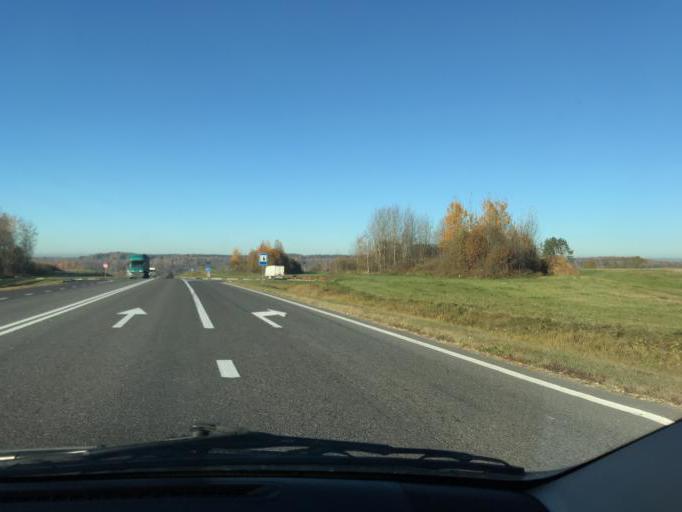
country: BY
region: Vitebsk
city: Vitebsk
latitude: 55.1048
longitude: 30.2283
